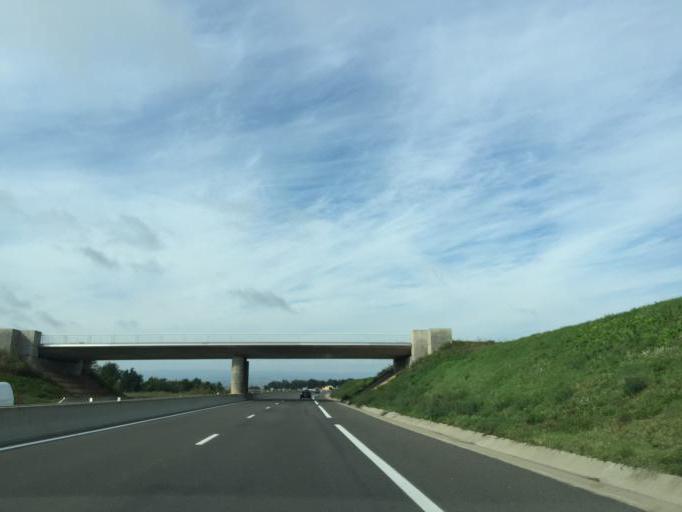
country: FR
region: Rhone-Alpes
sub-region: Departement de la Loire
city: Saint-Just-Saint-Rambert
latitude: 45.5157
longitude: 4.2392
